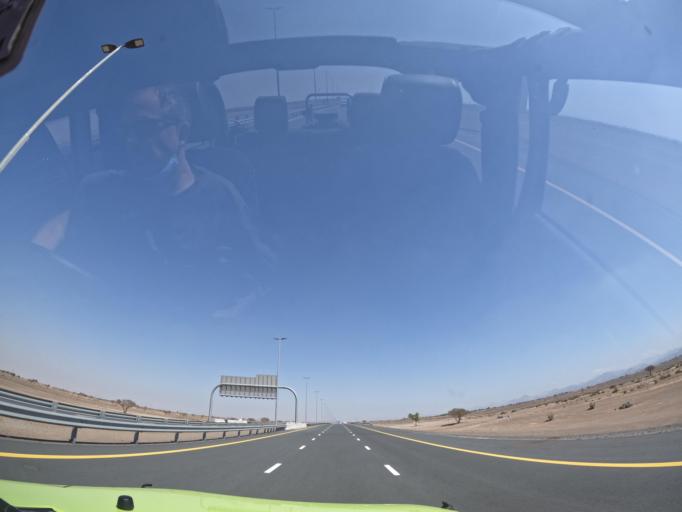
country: AE
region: Ash Shariqah
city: Adh Dhayd
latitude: 25.0830
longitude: 55.9165
